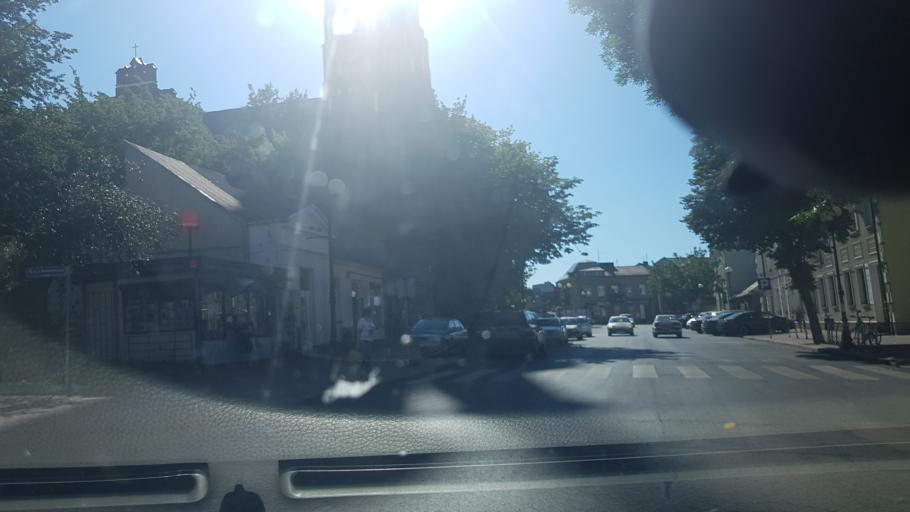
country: PL
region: Masovian Voivodeship
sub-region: Siedlce
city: Siedlce
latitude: 52.1697
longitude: 22.2753
